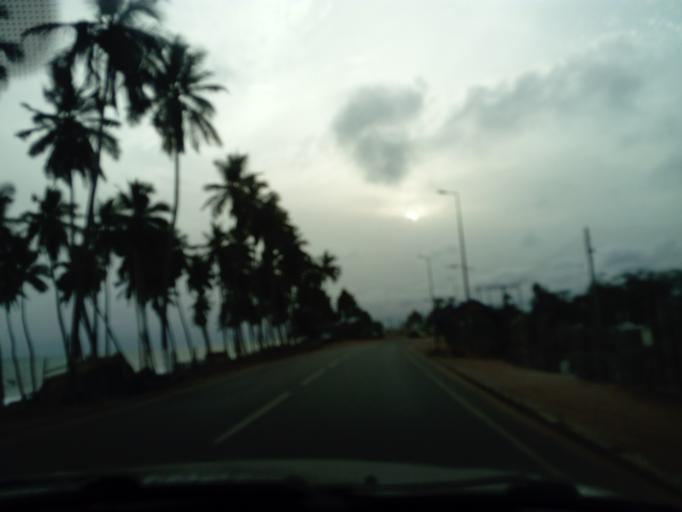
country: GH
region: Central
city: Cape Coast
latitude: 5.1007
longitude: -1.2817
